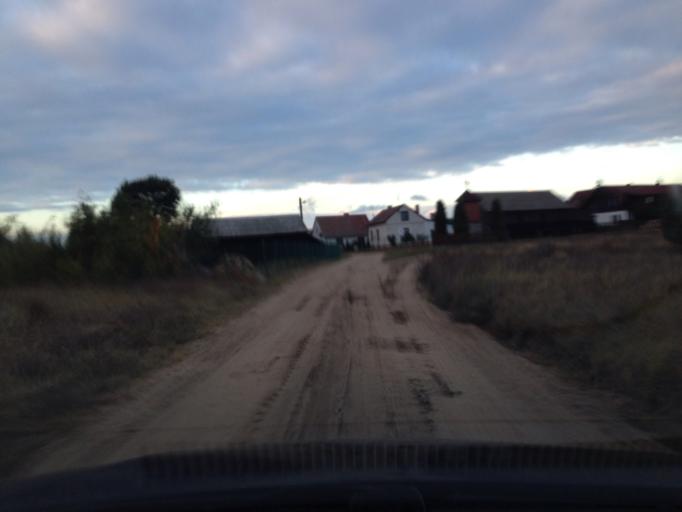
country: PL
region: Kujawsko-Pomorskie
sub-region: Powiat brodnicki
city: Gorzno
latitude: 53.1533
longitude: 19.6511
